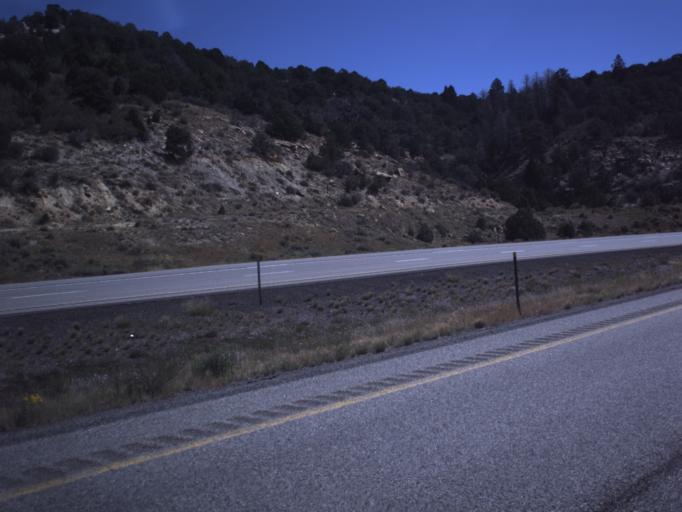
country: US
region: Utah
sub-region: Sevier County
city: Salina
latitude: 38.7955
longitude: -111.5089
